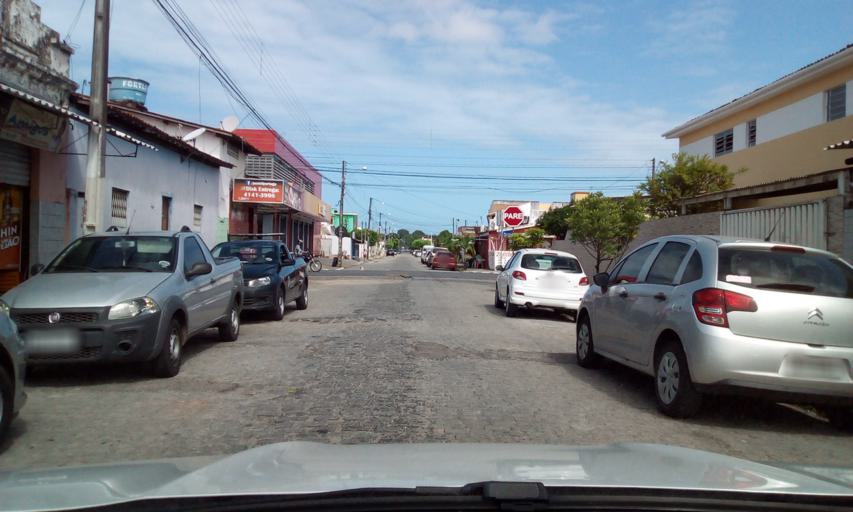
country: BR
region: Paraiba
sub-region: Joao Pessoa
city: Joao Pessoa
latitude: -7.1316
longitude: -34.8779
